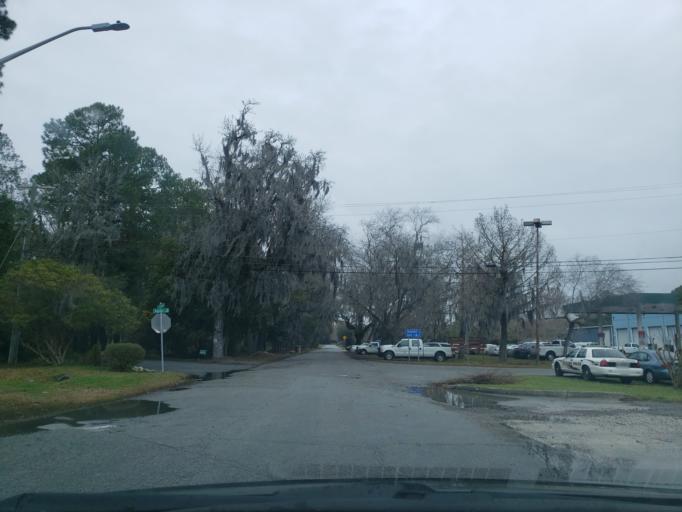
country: US
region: Georgia
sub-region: Chatham County
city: Isle of Hope
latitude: 32.0042
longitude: -81.0901
